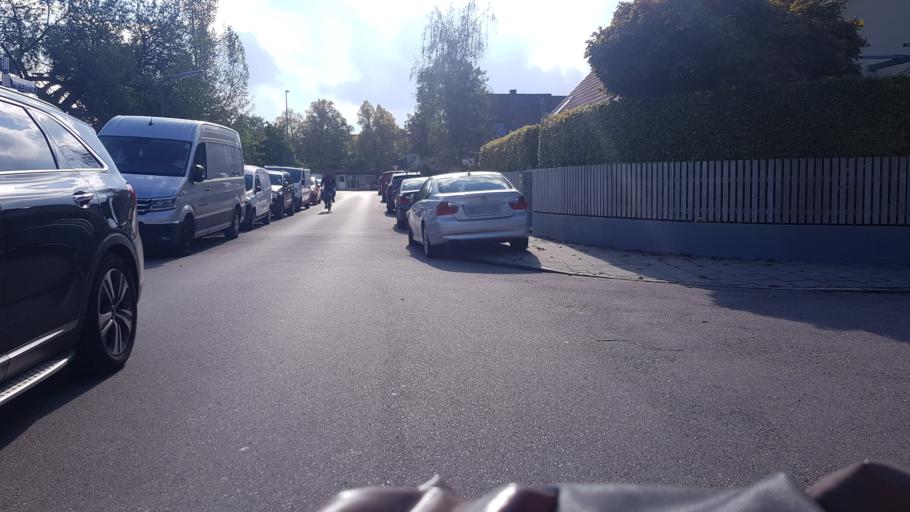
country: DE
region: Bavaria
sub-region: Upper Bavaria
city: Pasing
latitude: 48.1309
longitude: 11.4894
